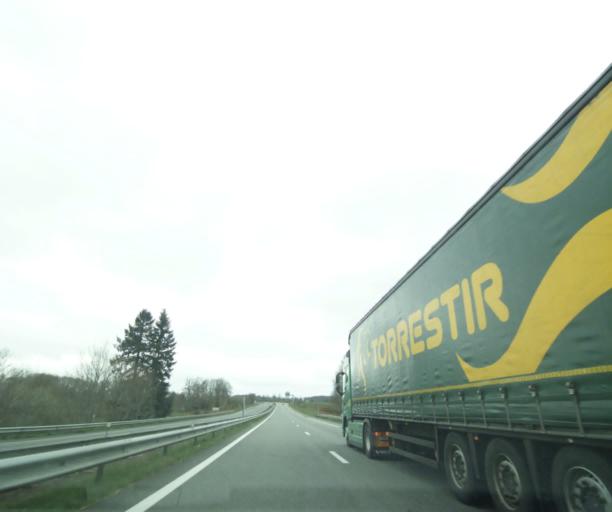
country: FR
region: Limousin
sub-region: Departement de la Creuse
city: Saint-Maurice-la-Souterraine
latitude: 46.2123
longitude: 1.3853
